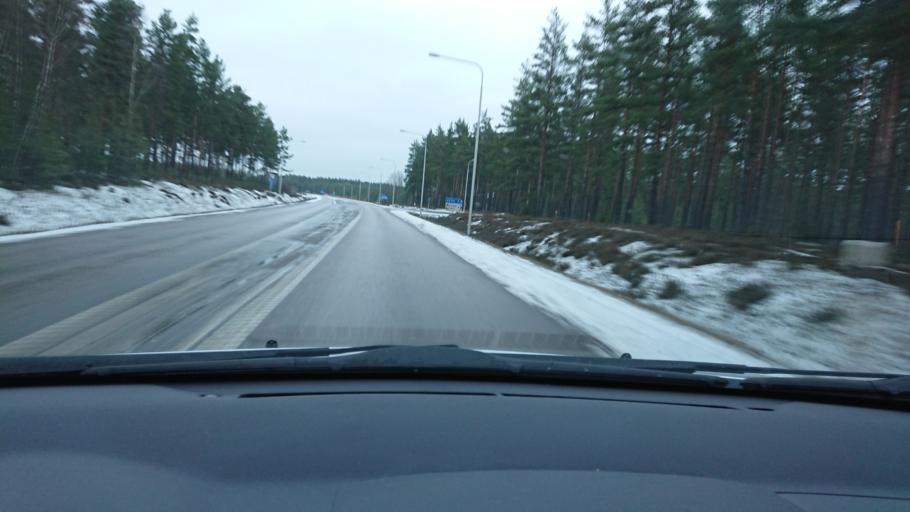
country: SE
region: Kalmar
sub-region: Hultsfreds Kommun
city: Hultsfred
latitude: 57.5162
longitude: 15.8419
